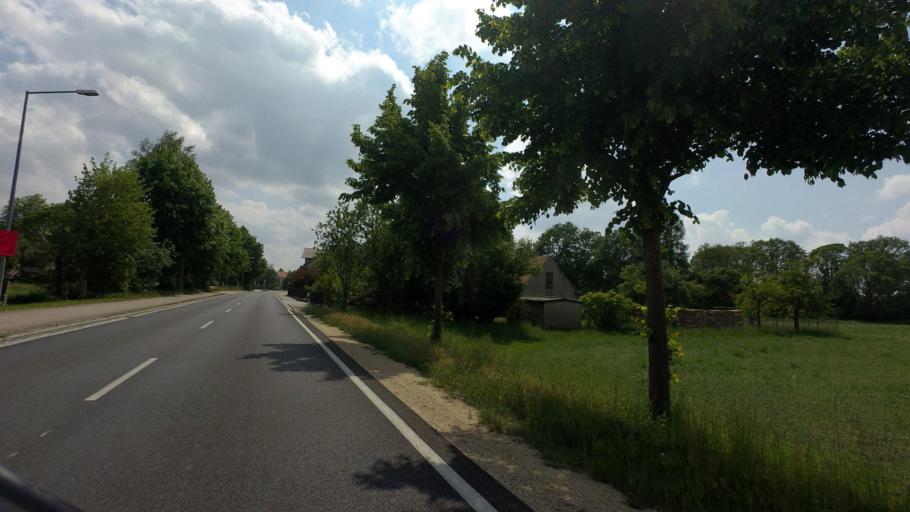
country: DE
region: Saxony
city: Rietschen
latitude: 51.4016
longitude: 14.7862
